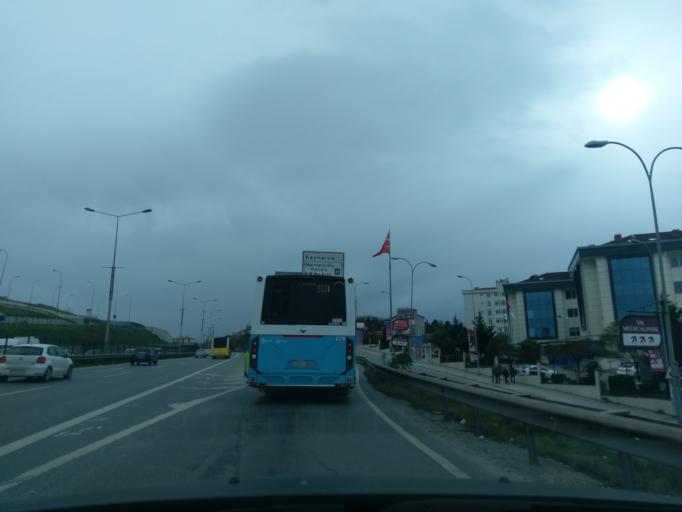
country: TR
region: Istanbul
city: Pendik
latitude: 40.8837
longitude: 29.2454
